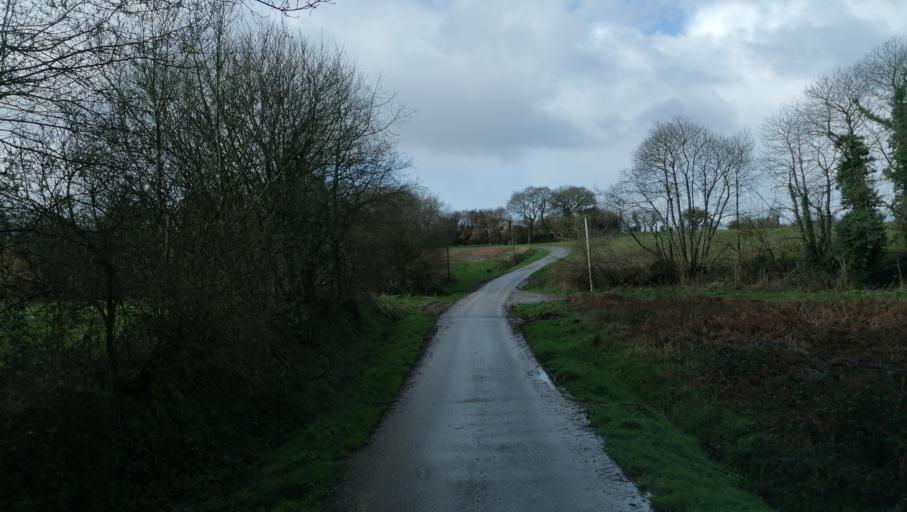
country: FR
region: Brittany
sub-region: Departement des Cotes-d'Armor
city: Lanrodec
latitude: 48.4852
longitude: -3.0335
